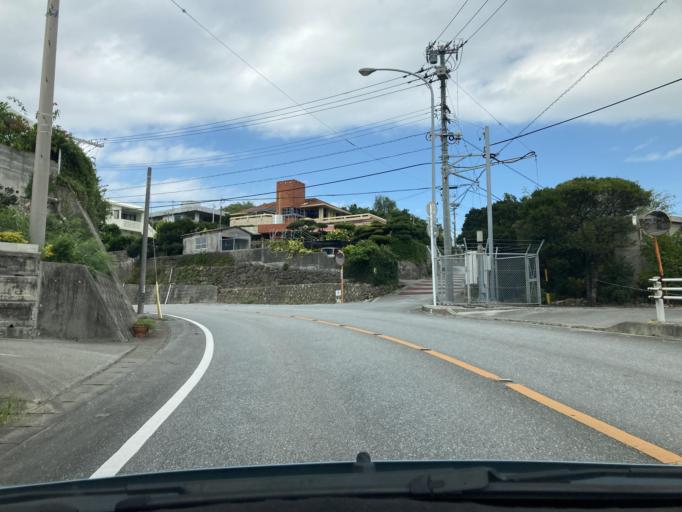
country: JP
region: Okinawa
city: Ginowan
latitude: 26.2680
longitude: 127.7860
